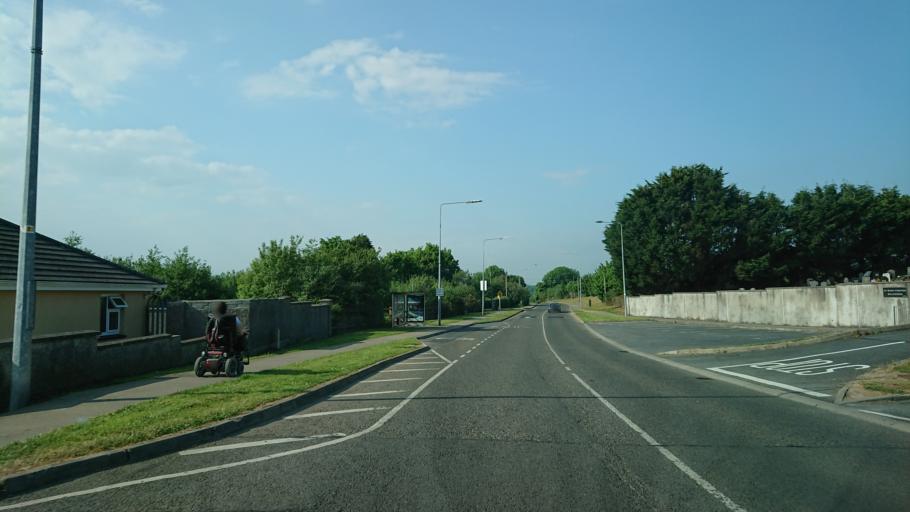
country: IE
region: Munster
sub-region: Waterford
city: Waterford
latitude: 52.2316
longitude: -7.0622
